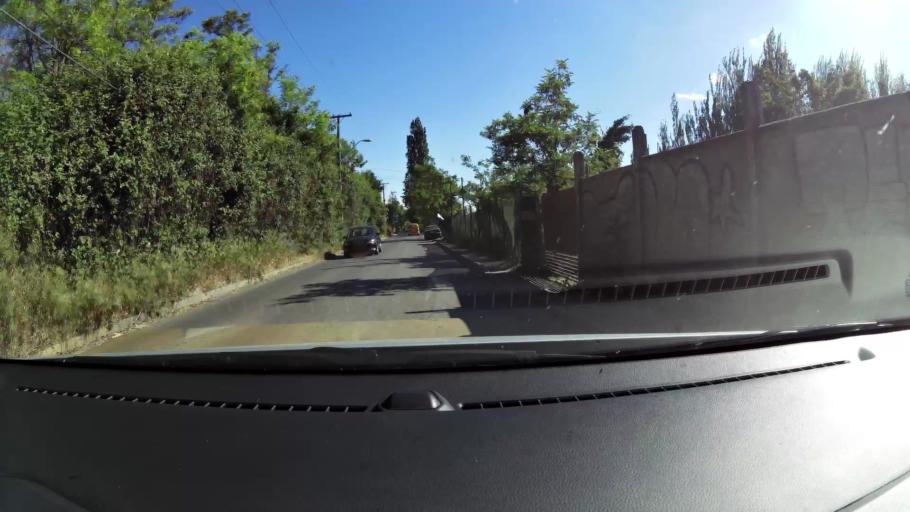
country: CL
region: Santiago Metropolitan
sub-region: Provincia de Maipo
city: San Bernardo
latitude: -33.5566
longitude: -70.7785
